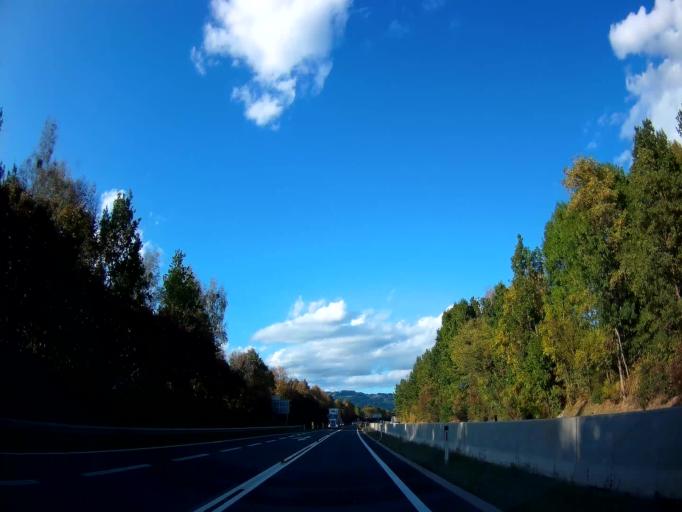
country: AT
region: Carinthia
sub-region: Politischer Bezirk Wolfsberg
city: Wolfsberg
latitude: 46.8244
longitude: 14.8194
